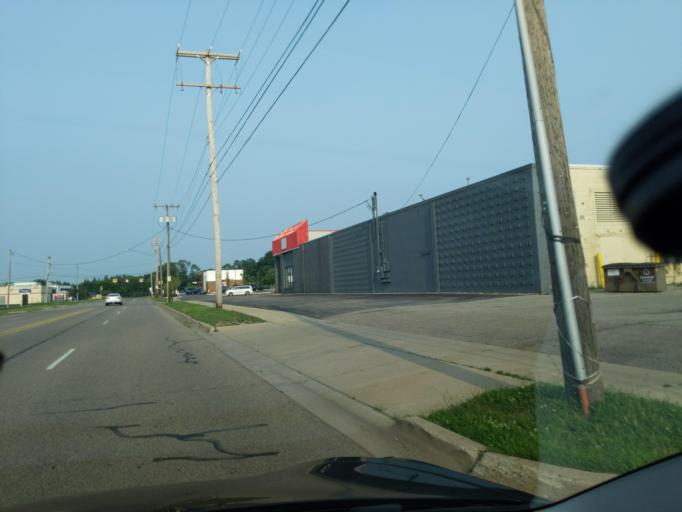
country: US
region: Michigan
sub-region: Jackson County
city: Jackson
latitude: 42.2620
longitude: -84.4257
